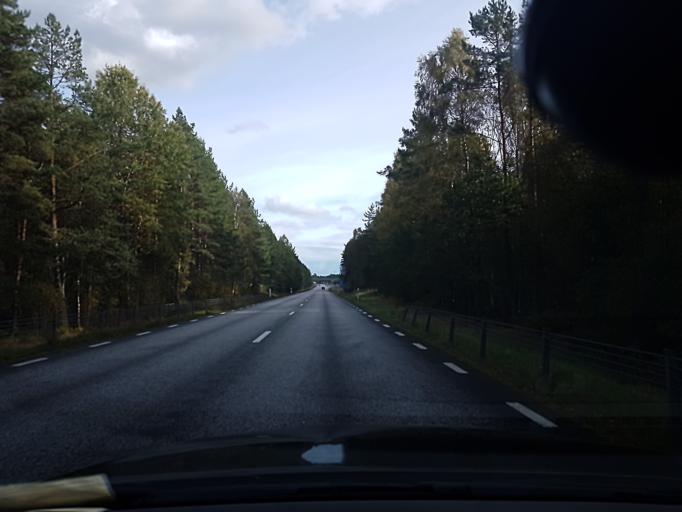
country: SE
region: Joenkoeping
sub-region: Varnamo Kommun
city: Bredaryd
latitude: 57.1838
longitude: 13.7388
